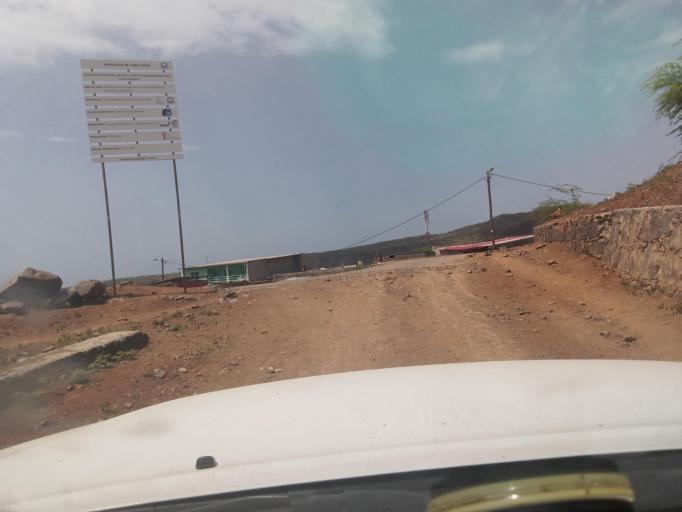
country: CV
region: Ribeira Grande de Santiago
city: Cidade Velha
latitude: 14.9868
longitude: -23.6346
